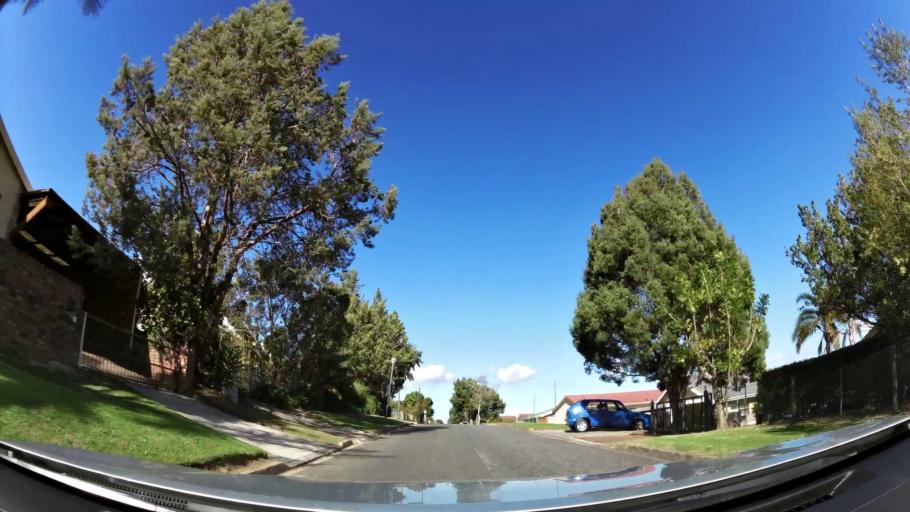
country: ZA
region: Western Cape
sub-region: Eden District Municipality
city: George
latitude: -33.9394
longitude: 22.4717
